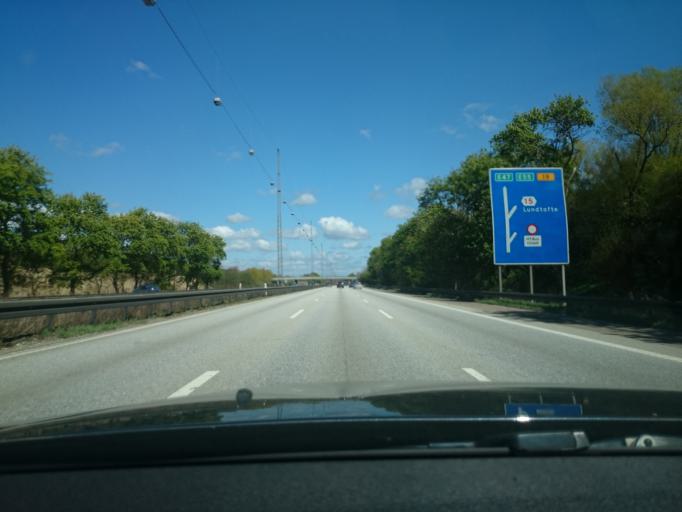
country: DK
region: Capital Region
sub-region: Lyngby-Tarbaek Kommune
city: Kongens Lyngby
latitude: 55.7841
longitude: 12.5278
